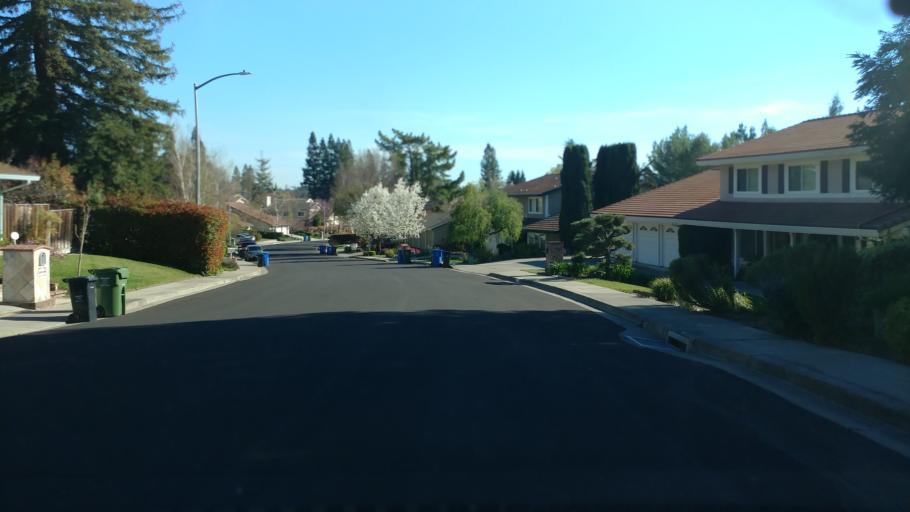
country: US
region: California
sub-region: Contra Costa County
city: San Ramon
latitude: 37.8056
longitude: -121.9749
